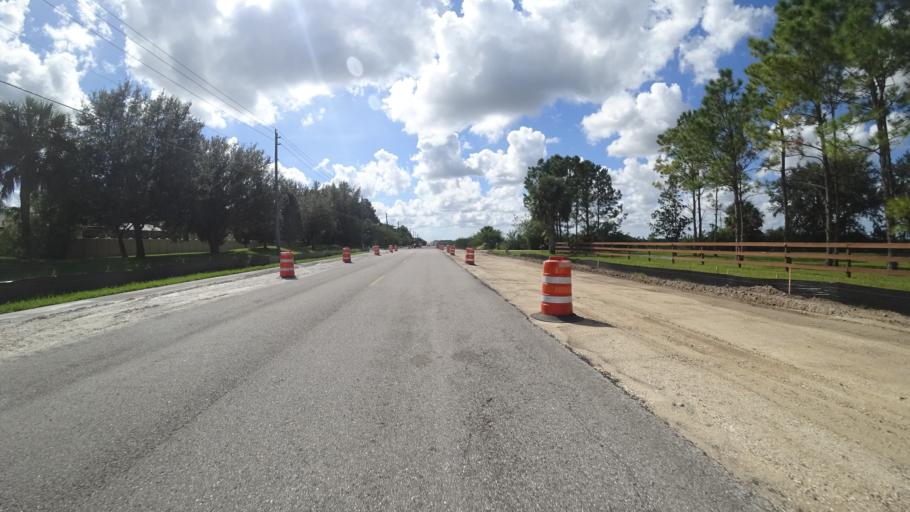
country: US
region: Florida
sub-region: Manatee County
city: Ellenton
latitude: 27.5073
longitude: -82.3715
